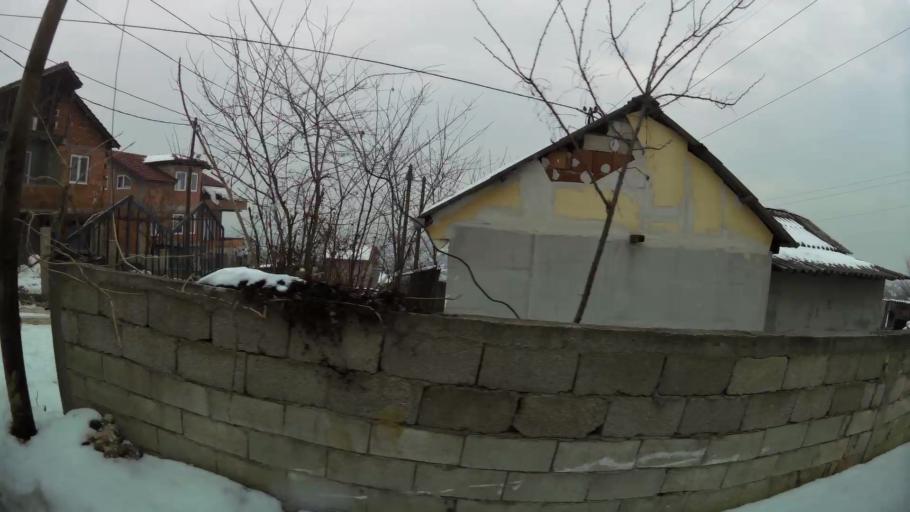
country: MK
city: Kondovo
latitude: 42.0396
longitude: 21.3439
